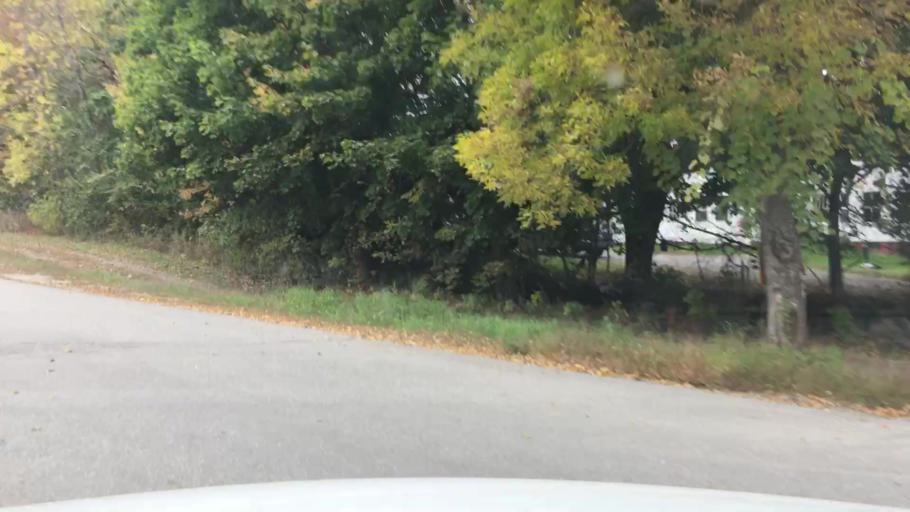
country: US
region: Maine
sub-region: Kennebec County
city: Oakland
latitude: 44.5666
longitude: -69.6809
